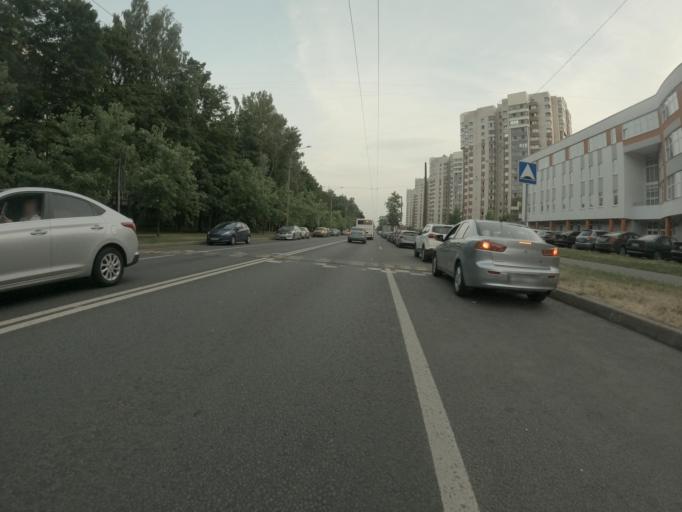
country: RU
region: Leningrad
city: Kalininskiy
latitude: 59.9826
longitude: 30.3975
